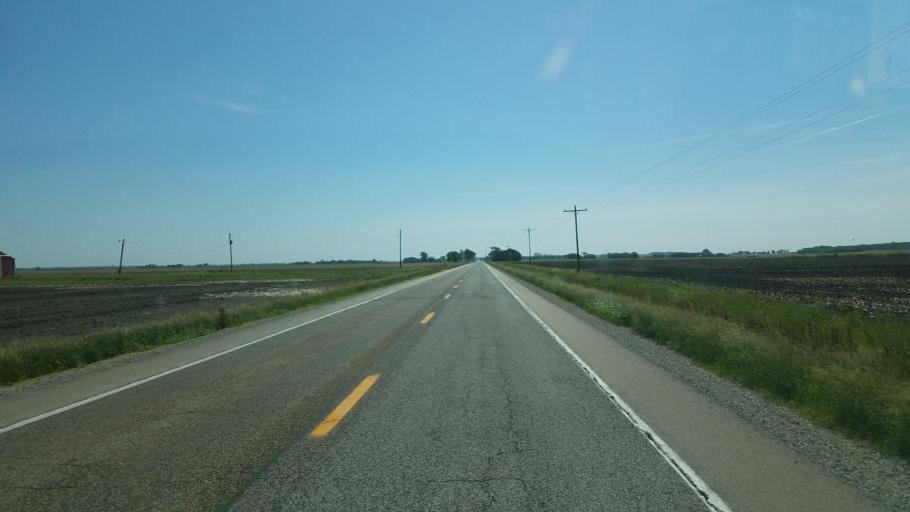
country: US
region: Illinois
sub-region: Mason County
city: Mason City
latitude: 40.3047
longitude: -89.7099
